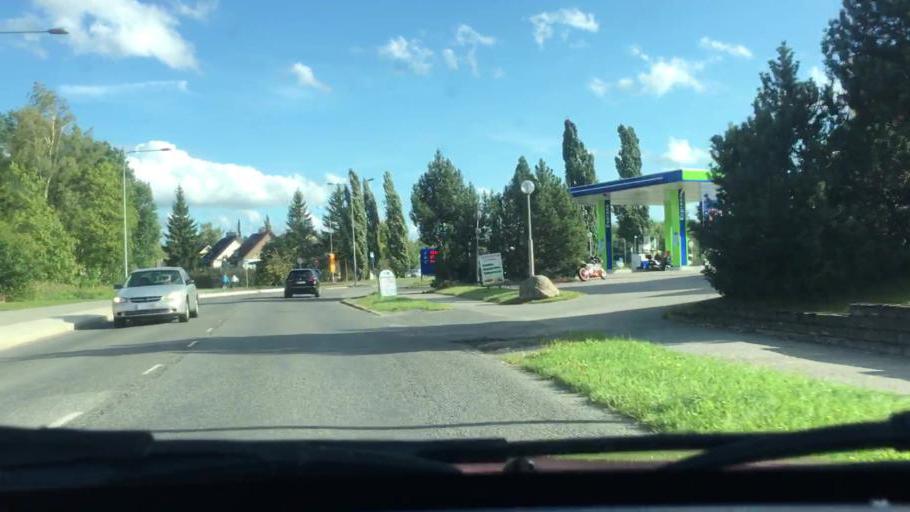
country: FI
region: Varsinais-Suomi
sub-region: Turku
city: Turku
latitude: 60.4711
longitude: 22.2350
